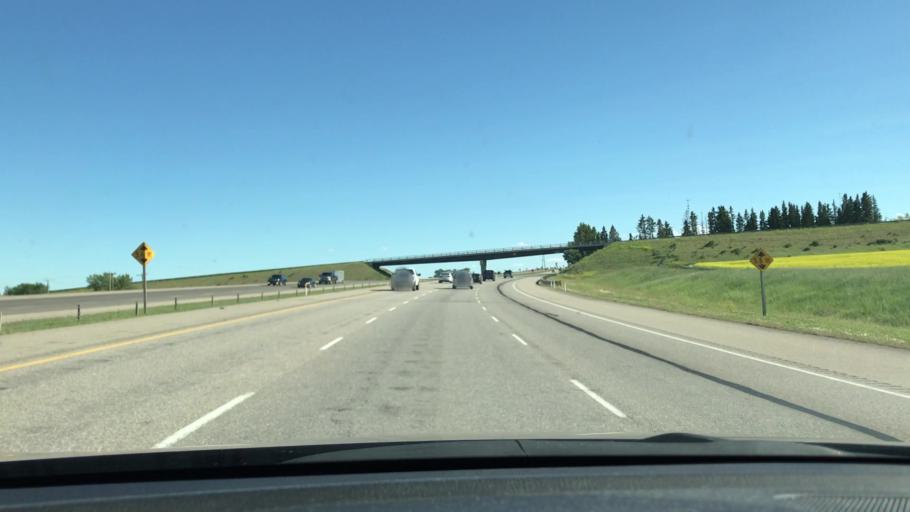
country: CA
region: Alberta
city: Crossfield
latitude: 51.4337
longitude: -114.0024
